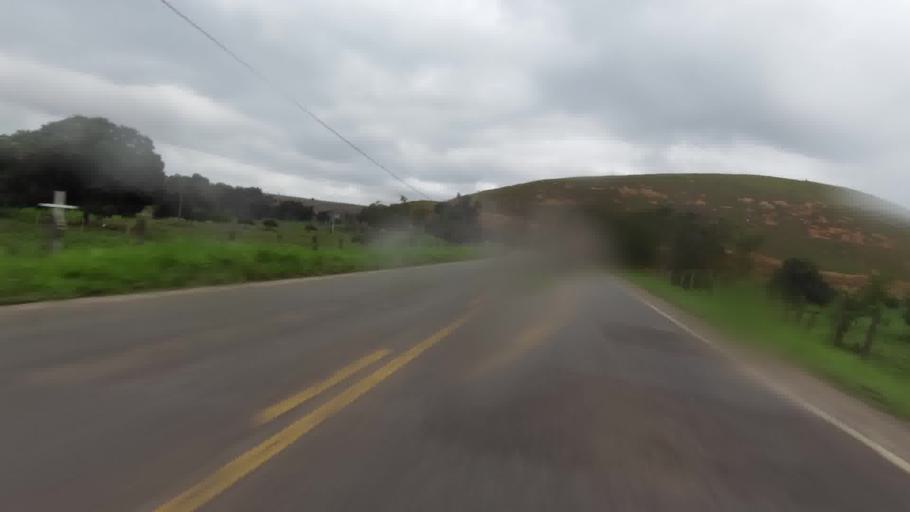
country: BR
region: Espirito Santo
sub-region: Alfredo Chaves
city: Alfredo Chaves
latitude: -20.6566
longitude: -40.7494
